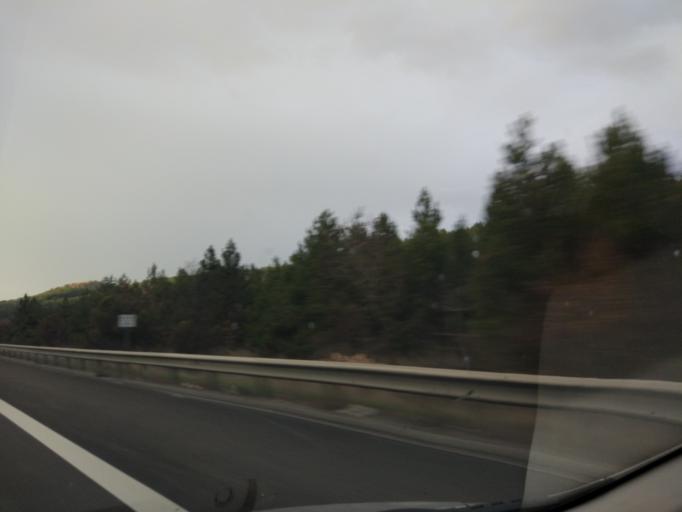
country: TR
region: Bolu
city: Bolu
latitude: 40.7369
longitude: 31.7985
